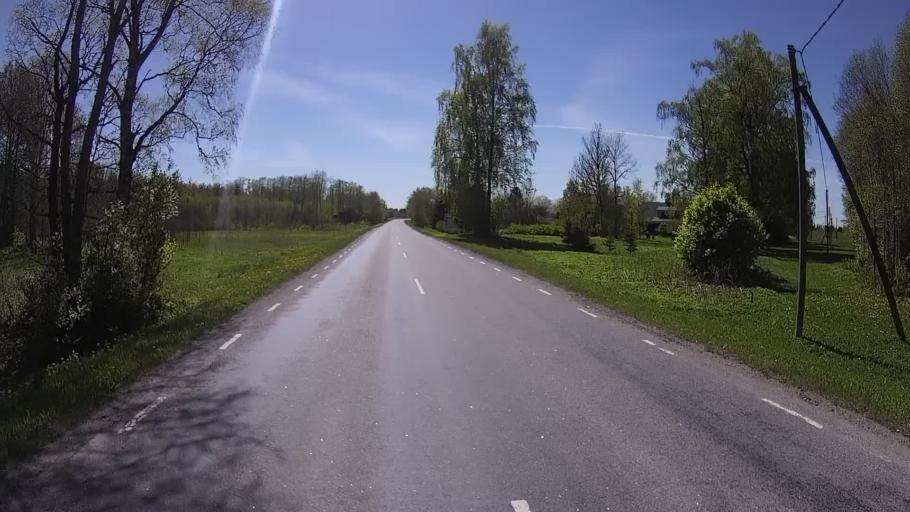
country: EE
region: Harju
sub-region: Rae vald
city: Vaida
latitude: 59.0691
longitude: 25.1566
